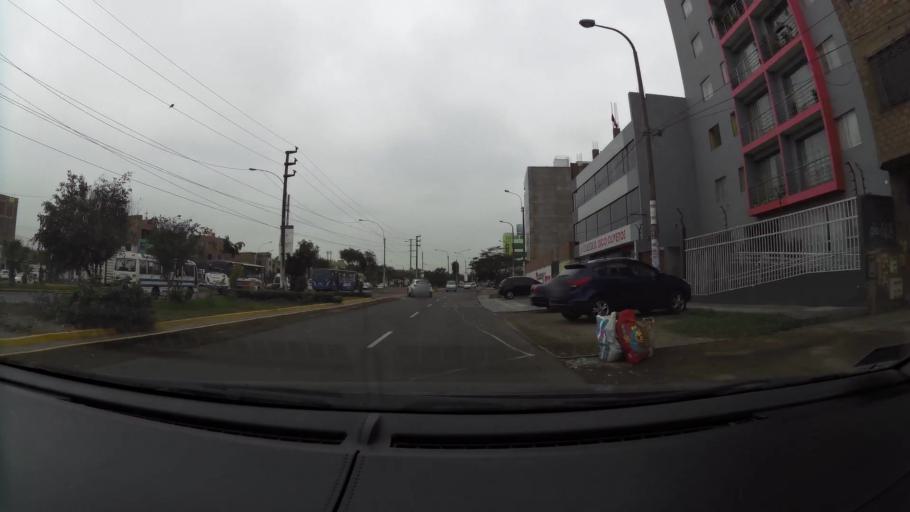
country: PE
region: Lima
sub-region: Lima
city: Independencia
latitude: -11.9655
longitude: -77.0733
